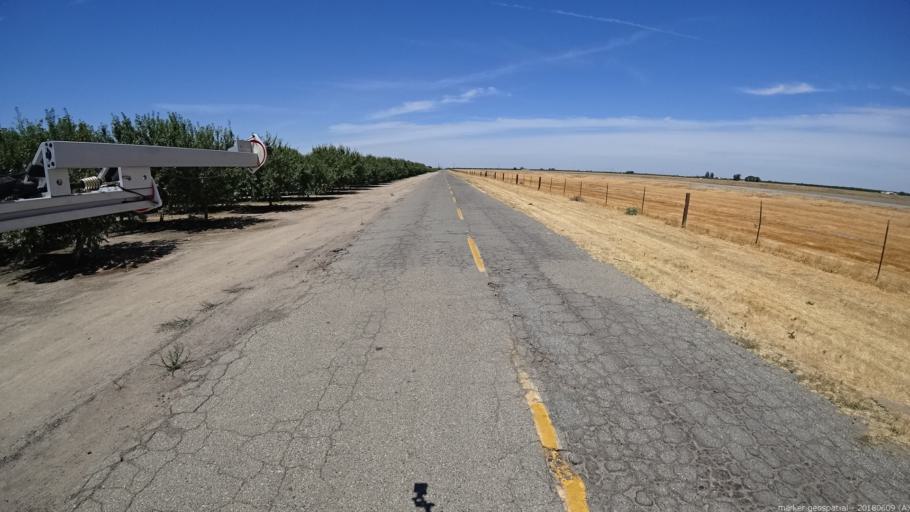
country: US
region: California
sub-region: Madera County
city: Madera
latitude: 36.9382
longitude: -120.1677
